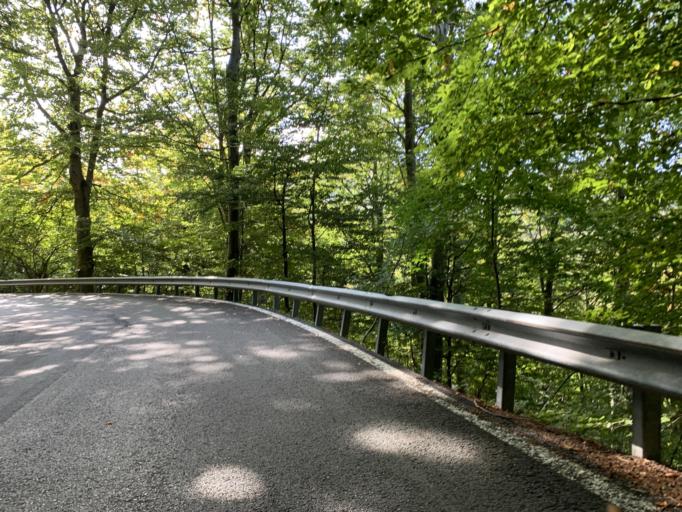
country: IT
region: Liguria
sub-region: Provincia di Savona
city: Osiglia
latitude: 44.2331
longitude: 8.1951
